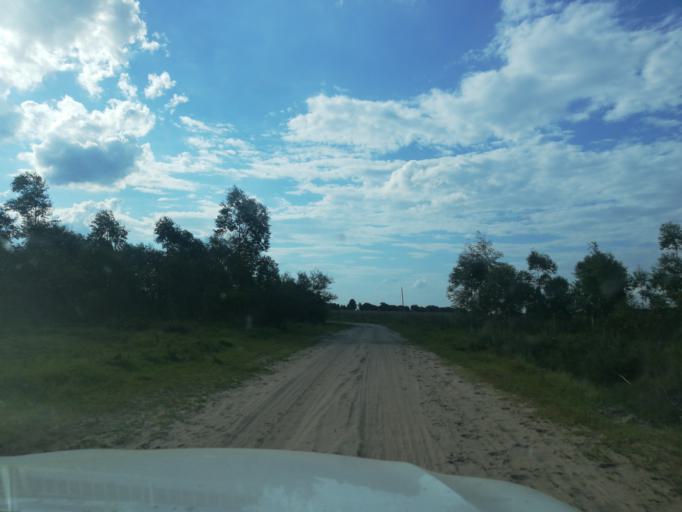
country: AR
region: Corrientes
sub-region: Departamento de San Miguel
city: San Miguel
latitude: -27.9900
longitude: -57.5676
